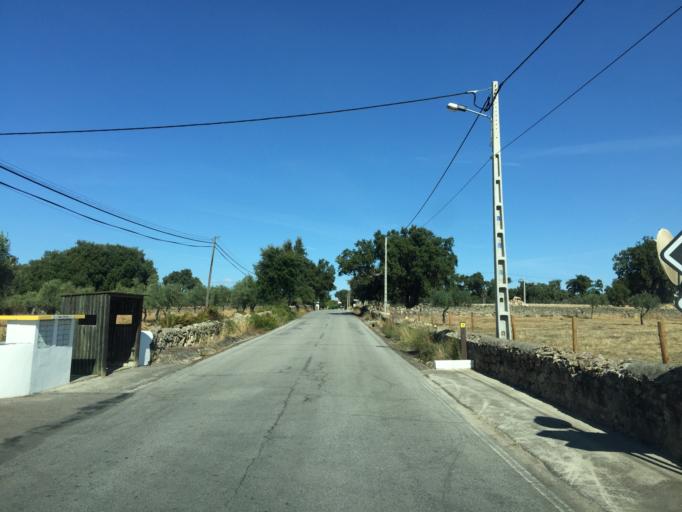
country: PT
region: Portalegre
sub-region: Marvao
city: Marvao
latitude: 39.4287
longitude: -7.3571
